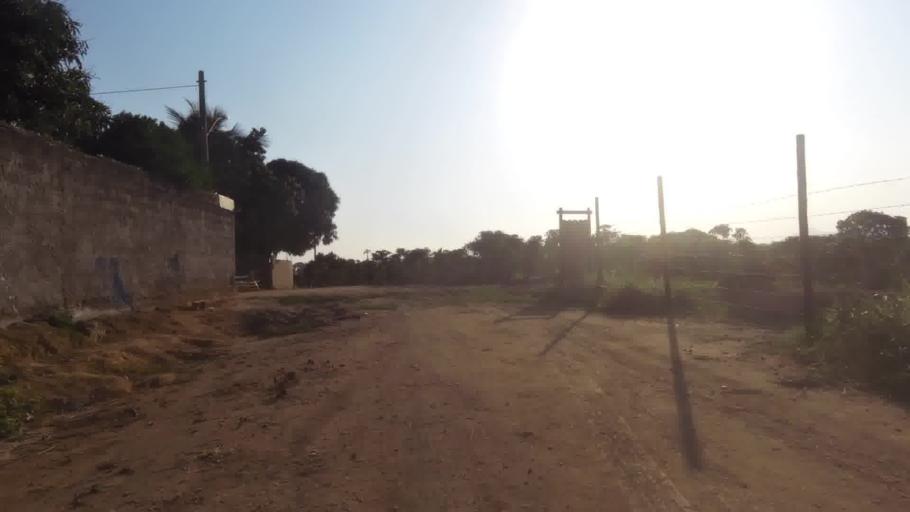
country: BR
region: Espirito Santo
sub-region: Piuma
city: Piuma
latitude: -20.8220
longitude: -40.7186
